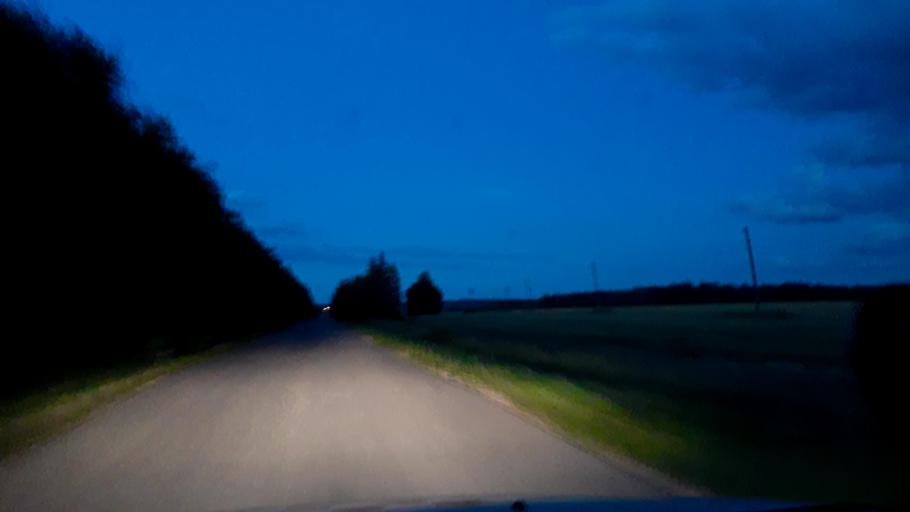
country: RU
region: Nizjnij Novgorod
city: Pamyat' Parizhskoy Kommuny
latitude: 56.0596
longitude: 44.4752
